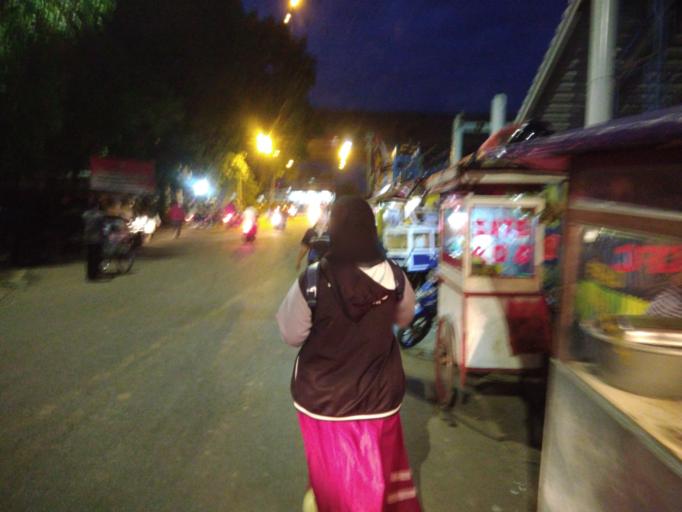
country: ID
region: West Java
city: Bekasi
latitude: -6.2188
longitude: 106.9524
